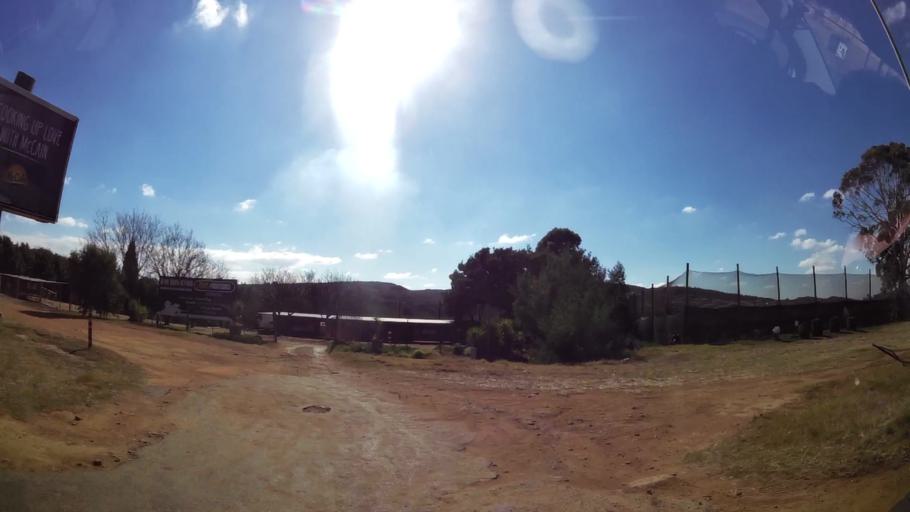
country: ZA
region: Gauteng
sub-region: West Rand District Municipality
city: Krugersdorp
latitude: -26.0895
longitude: 27.8199
